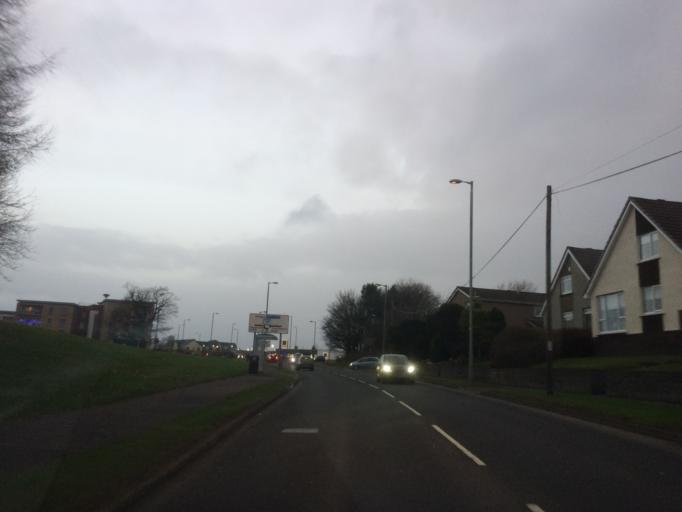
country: GB
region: Scotland
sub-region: East Renfrewshire
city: Newton Mearns
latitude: 55.7823
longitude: -4.3431
